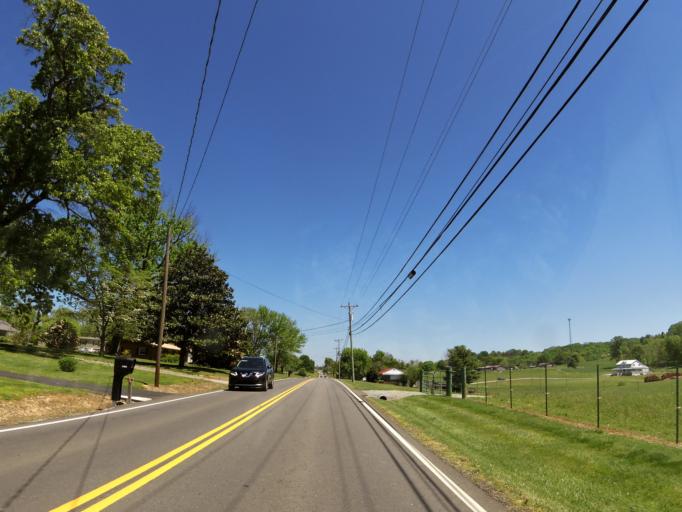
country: US
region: Tennessee
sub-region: Greene County
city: Greeneville
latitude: 36.1347
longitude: -82.8822
